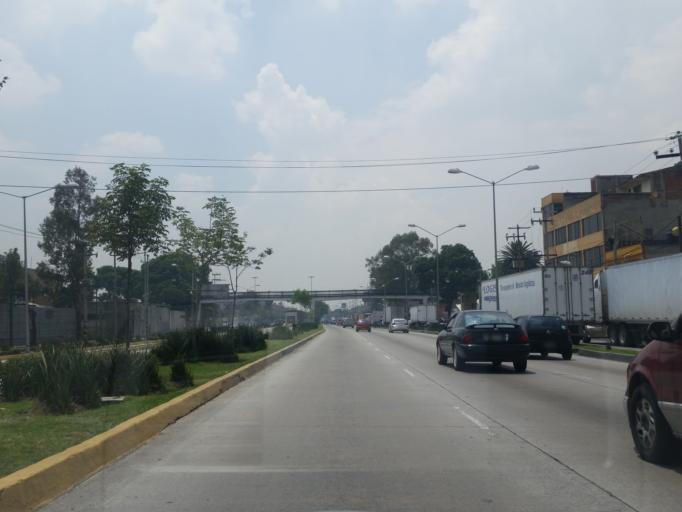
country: MX
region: Mexico City
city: Azcapotzalco
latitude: 19.5111
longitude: -99.1603
